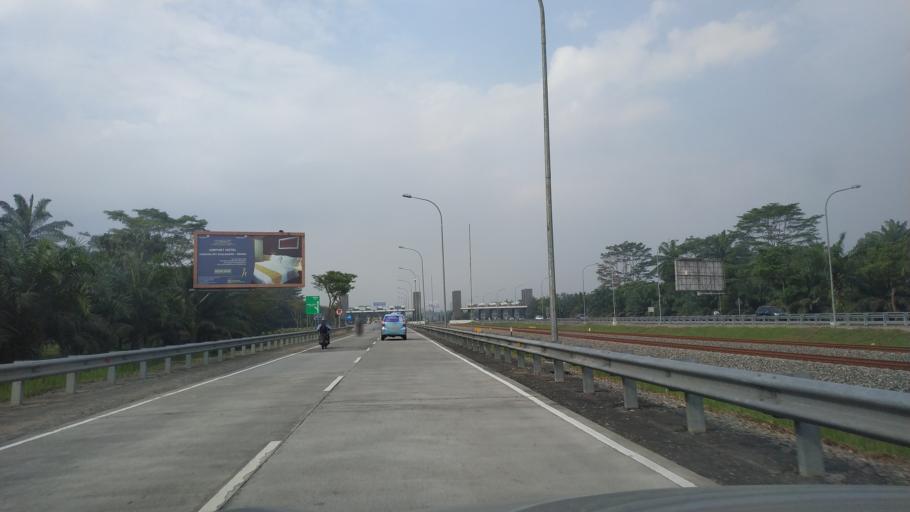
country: ID
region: North Sumatra
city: Percut
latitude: 3.6158
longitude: 98.8597
